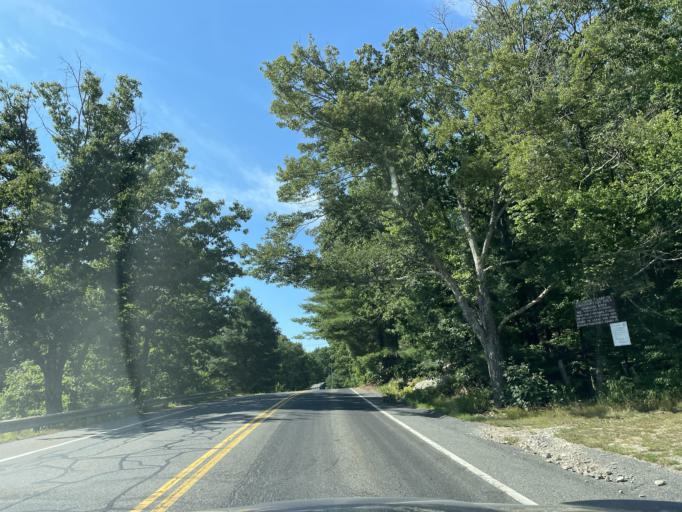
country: US
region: Massachusetts
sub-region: Worcester County
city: Northbridge
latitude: 42.1500
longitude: -71.6408
